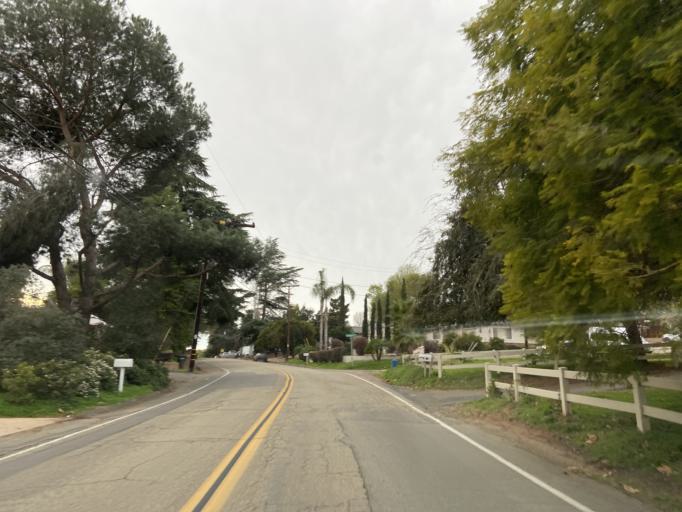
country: US
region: California
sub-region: San Diego County
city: Escondido
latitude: 33.1047
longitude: -117.0637
